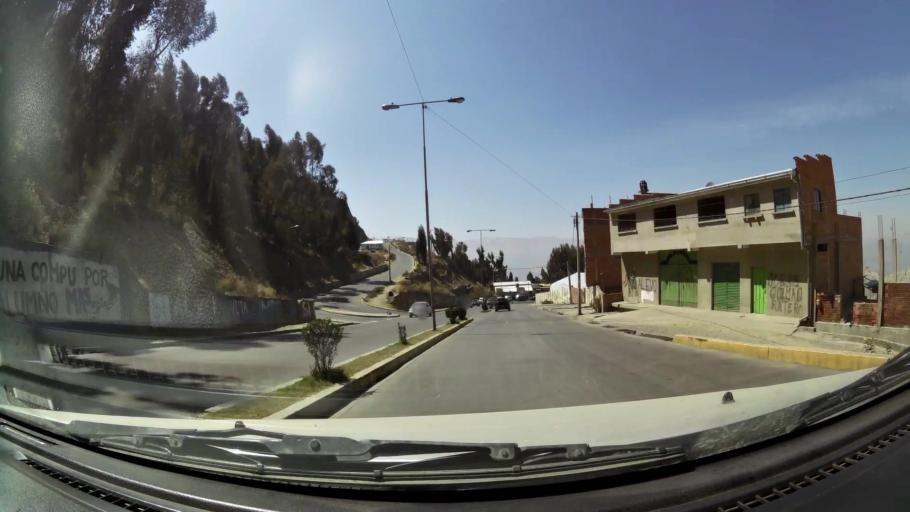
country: BO
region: La Paz
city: La Paz
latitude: -16.5306
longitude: -68.1454
